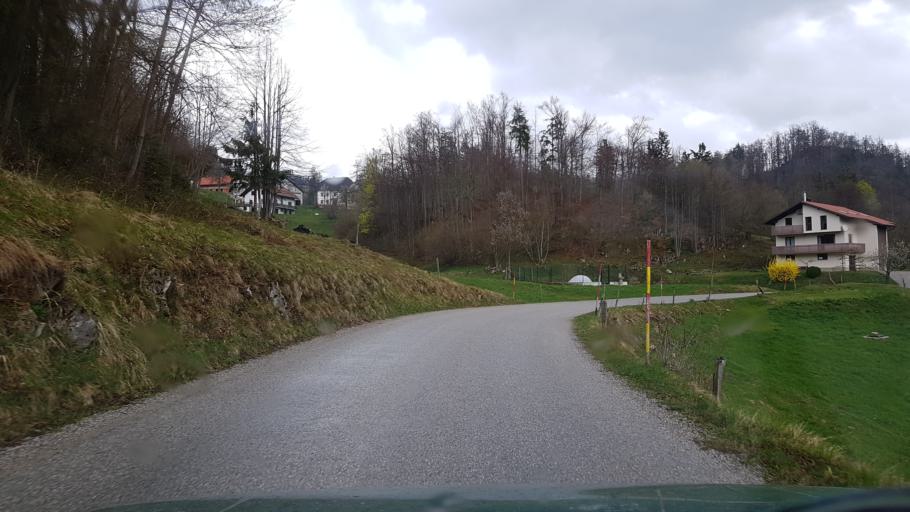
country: SI
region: Cerkno
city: Cerkno
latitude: 46.1136
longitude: 13.8516
